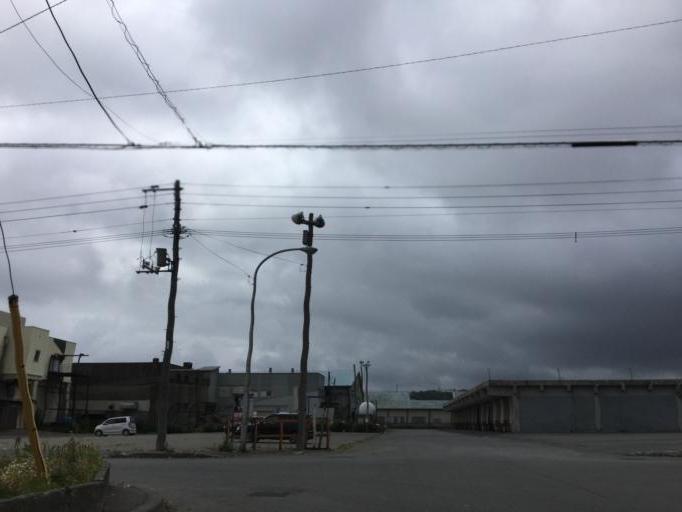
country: JP
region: Hokkaido
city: Wakkanai
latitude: 45.4082
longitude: 141.6797
